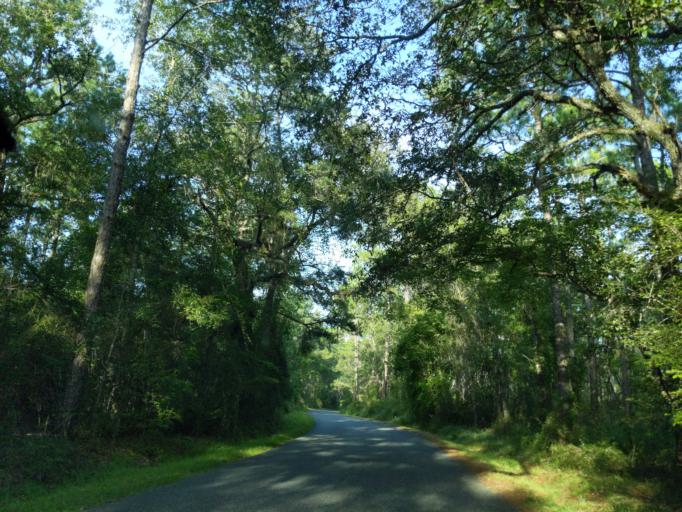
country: US
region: Florida
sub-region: Leon County
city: Tallahassee
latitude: 30.3448
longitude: -84.3815
